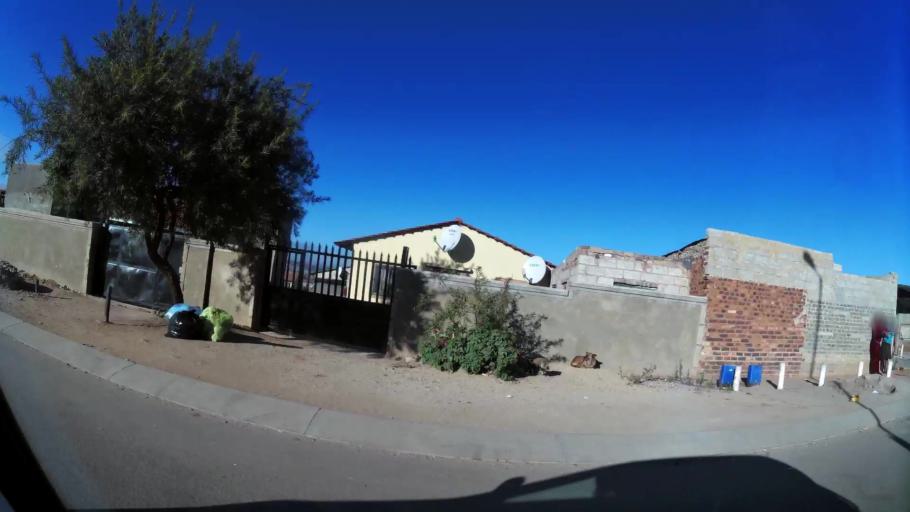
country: ZA
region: Gauteng
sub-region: City of Johannesburg Metropolitan Municipality
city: Diepsloot
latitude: -25.9033
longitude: 28.0976
